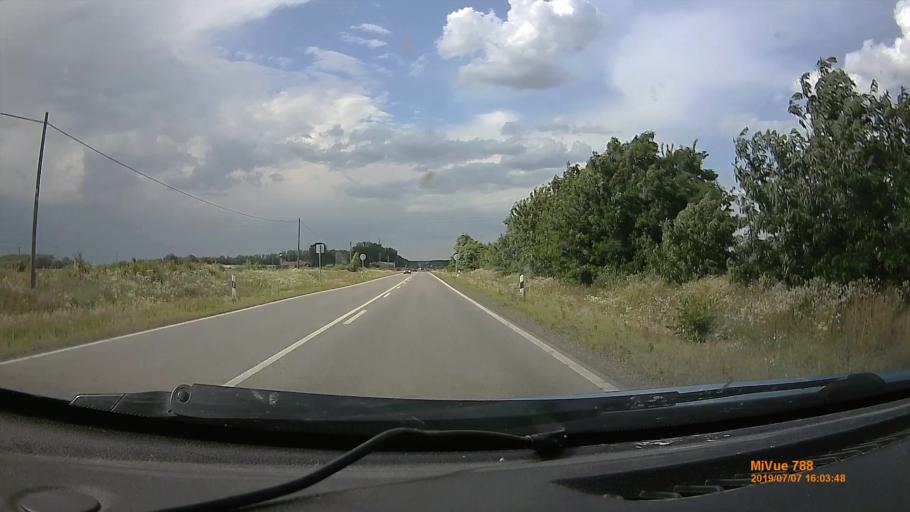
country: HU
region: Heves
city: Hatvan
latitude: 47.6437
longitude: 19.7275
